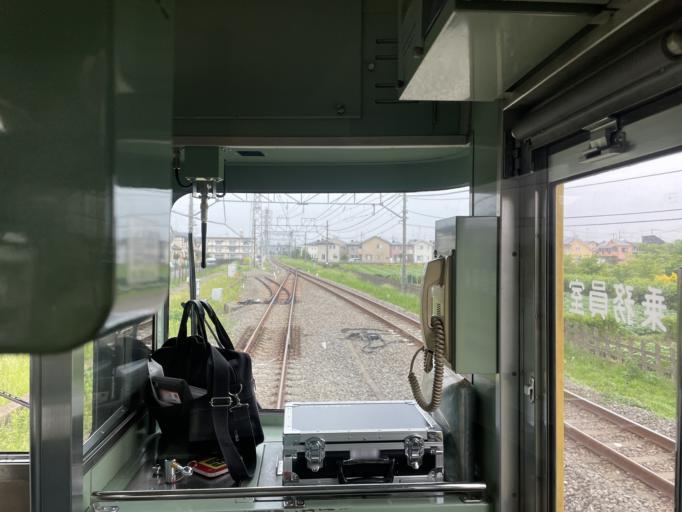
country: JP
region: Tokyo
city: Fussa
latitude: 35.7262
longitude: 139.3683
